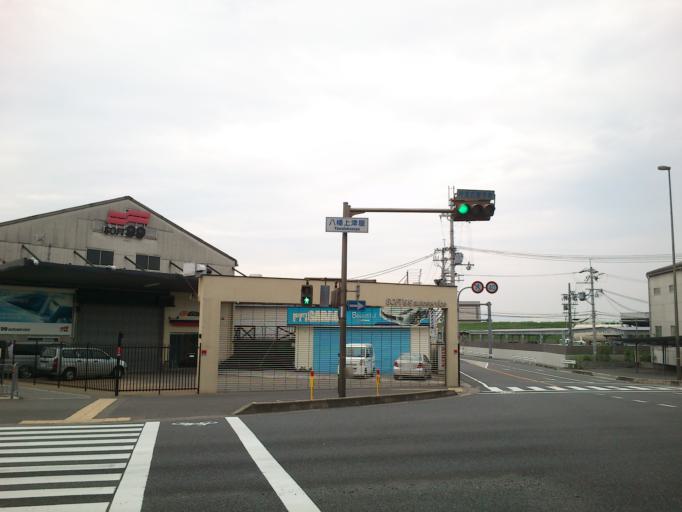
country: JP
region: Kyoto
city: Yawata
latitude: 34.8673
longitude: 135.7388
